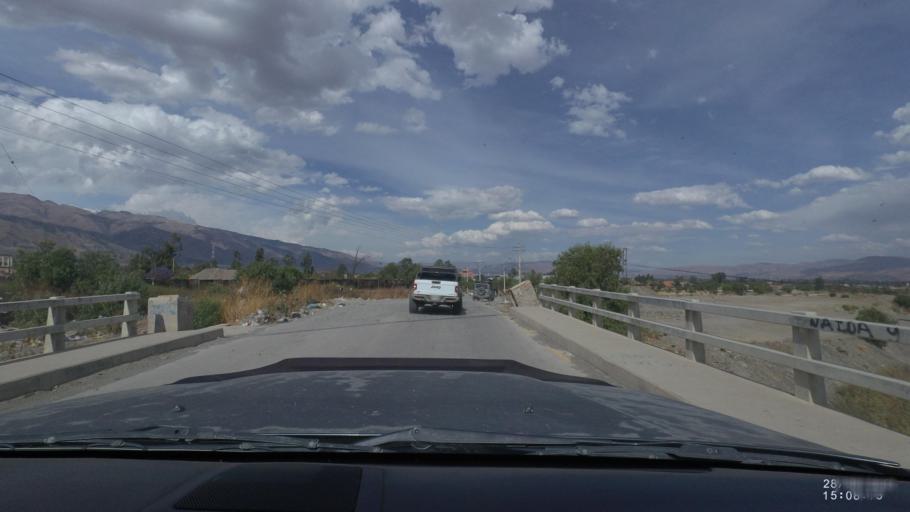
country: BO
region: Cochabamba
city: Cochabamba
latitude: -17.3375
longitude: -66.2762
